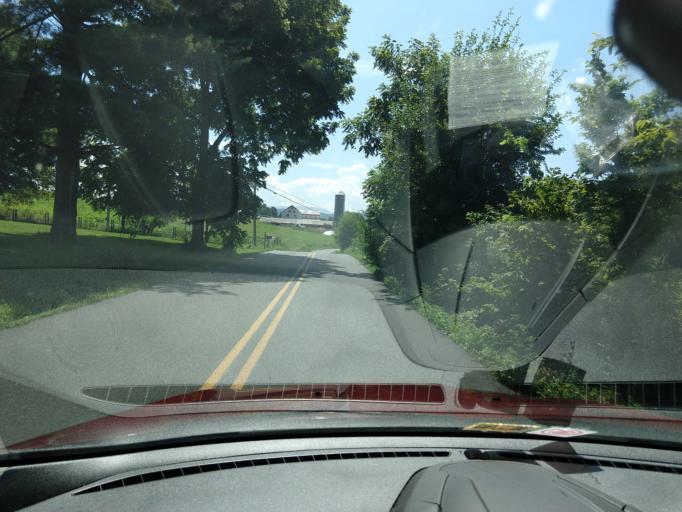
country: US
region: Virginia
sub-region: City of Harrisonburg
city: Harrisonburg
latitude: 38.5303
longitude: -78.8670
